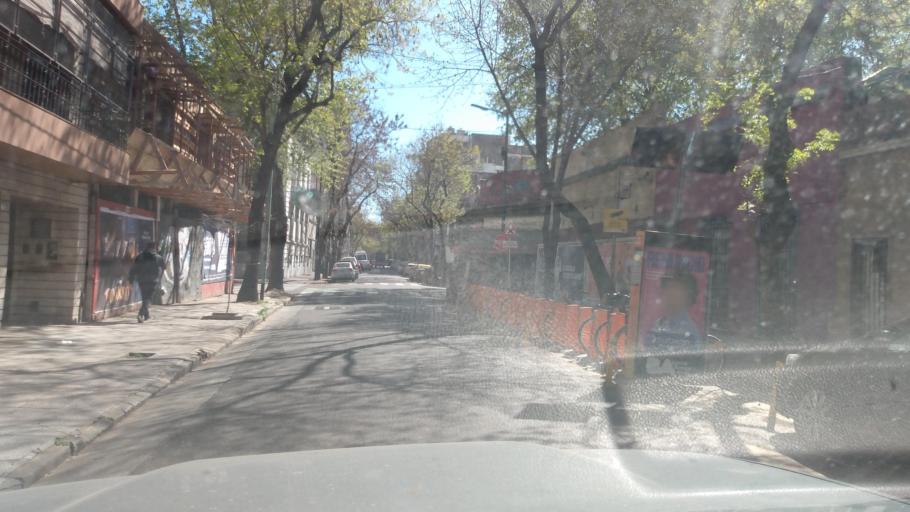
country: AR
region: Buenos Aires F.D.
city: Buenos Aires
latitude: -34.6209
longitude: -58.3945
